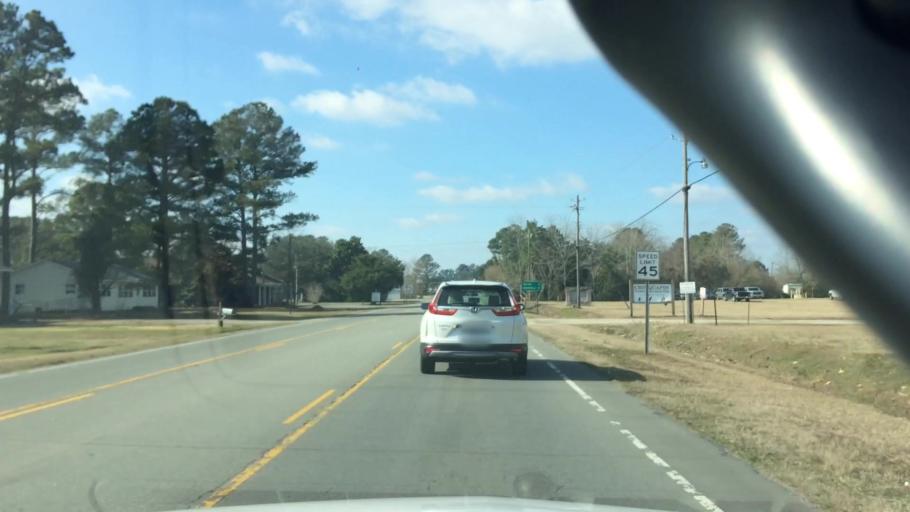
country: US
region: North Carolina
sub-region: Duplin County
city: Beulaville
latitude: 34.8298
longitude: -77.8132
